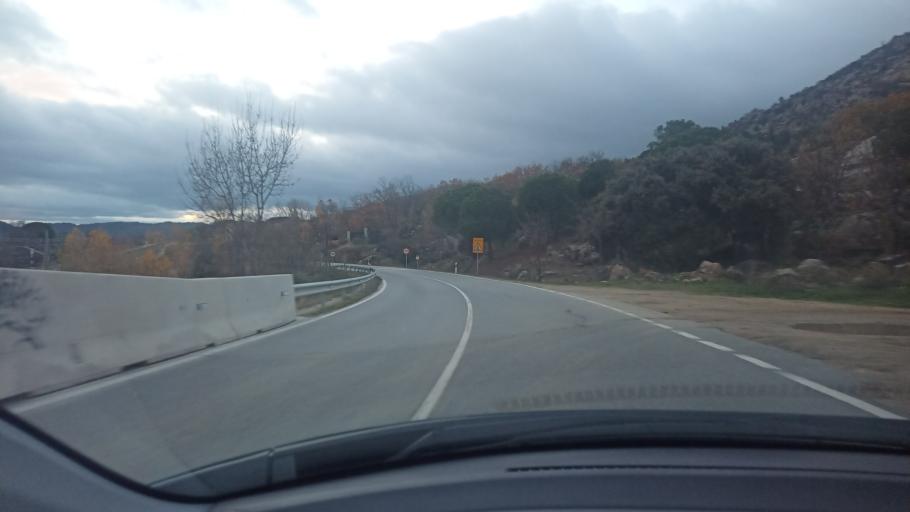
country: ES
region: Madrid
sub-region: Provincia de Madrid
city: Zarzalejo
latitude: 40.5403
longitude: -4.1527
